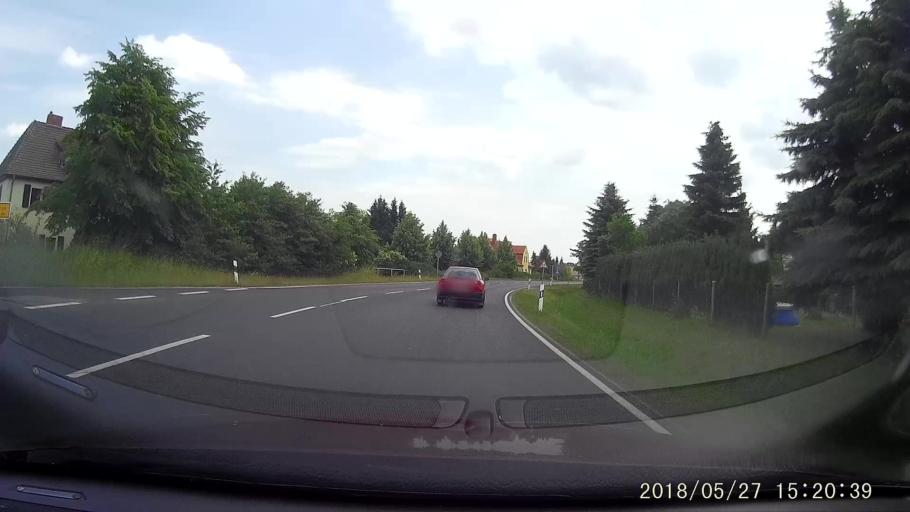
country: DE
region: Saxony
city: Kodersdorf
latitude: 51.2466
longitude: 14.8887
